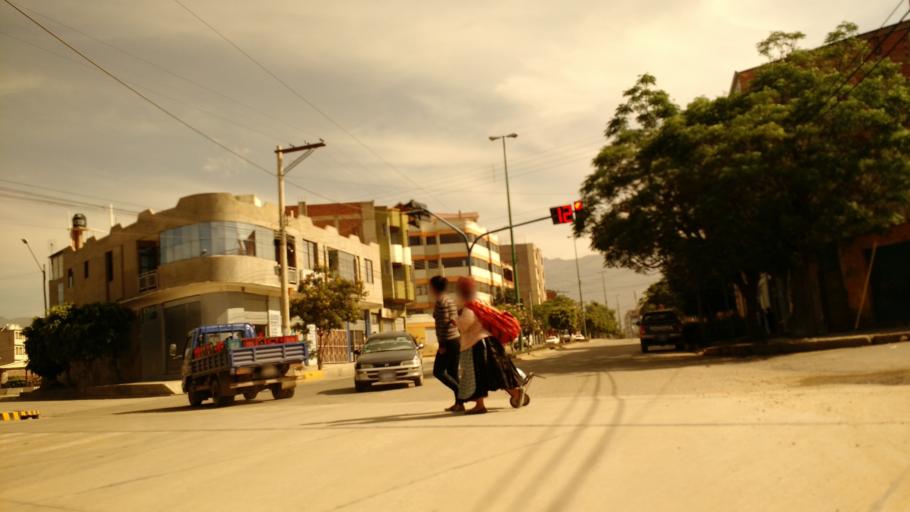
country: BO
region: Cochabamba
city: Cochabamba
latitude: -17.4277
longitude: -66.1592
